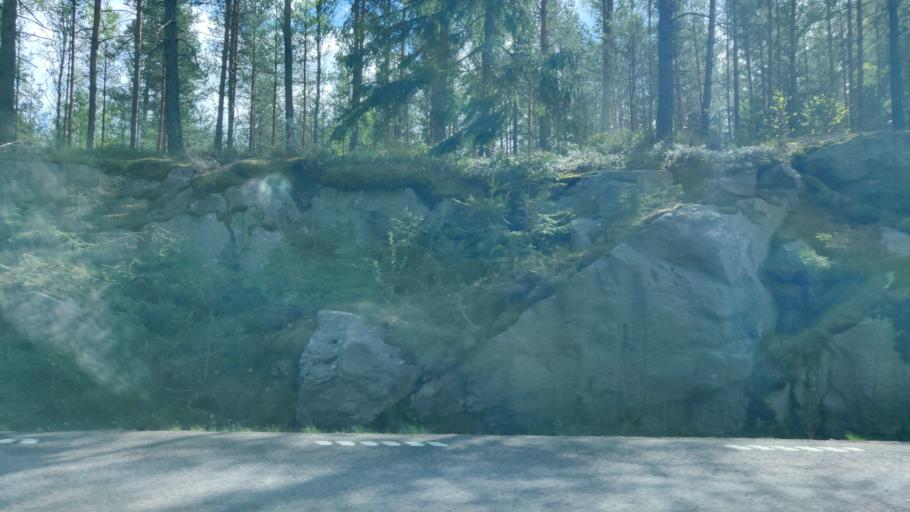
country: SE
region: Vaermland
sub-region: Karlstads Kommun
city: Molkom
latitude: 59.5826
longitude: 13.6761
